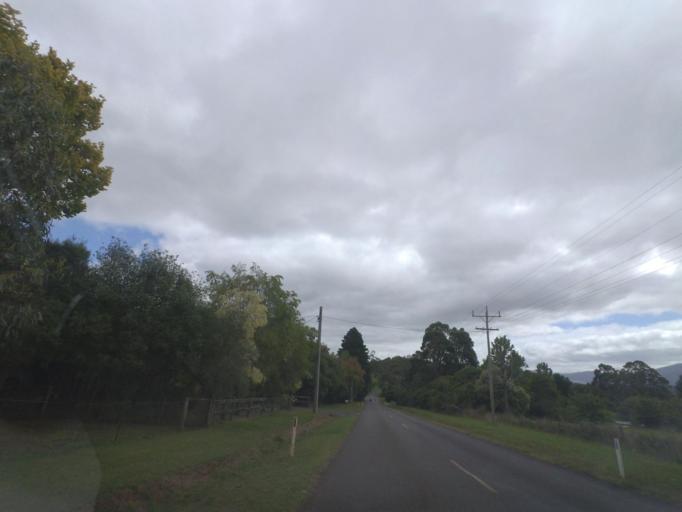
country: AU
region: Victoria
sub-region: Yarra Ranges
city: Launching Place
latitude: -37.8368
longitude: 145.5854
